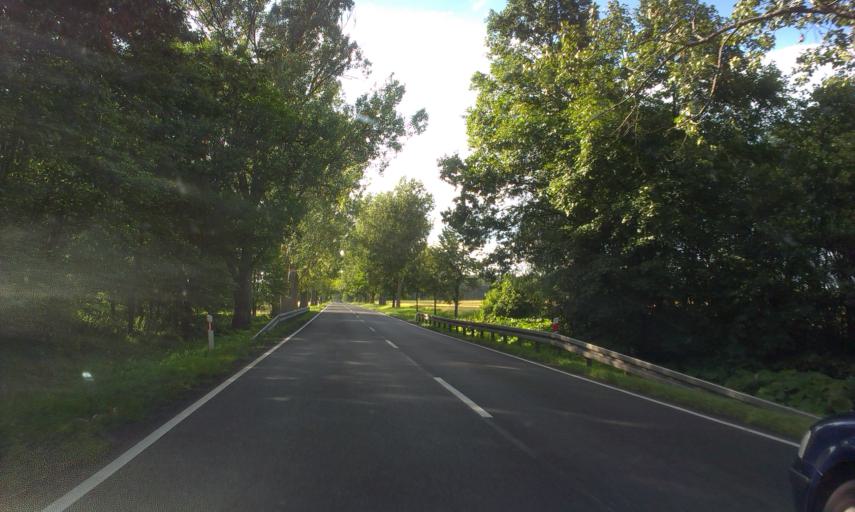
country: PL
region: Greater Poland Voivodeship
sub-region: Powiat zlotowski
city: Okonek
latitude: 53.4827
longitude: 16.8720
